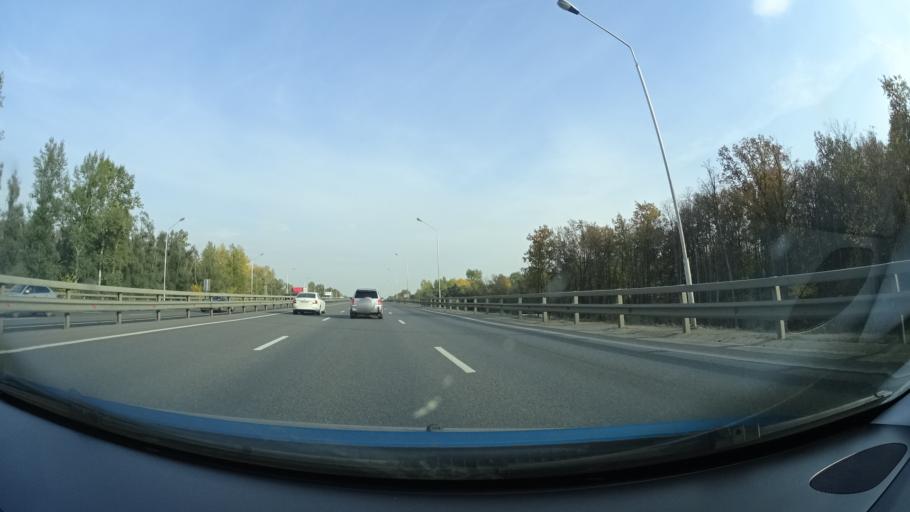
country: RU
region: Bashkortostan
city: Ufa
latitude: 54.6631
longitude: 55.8695
